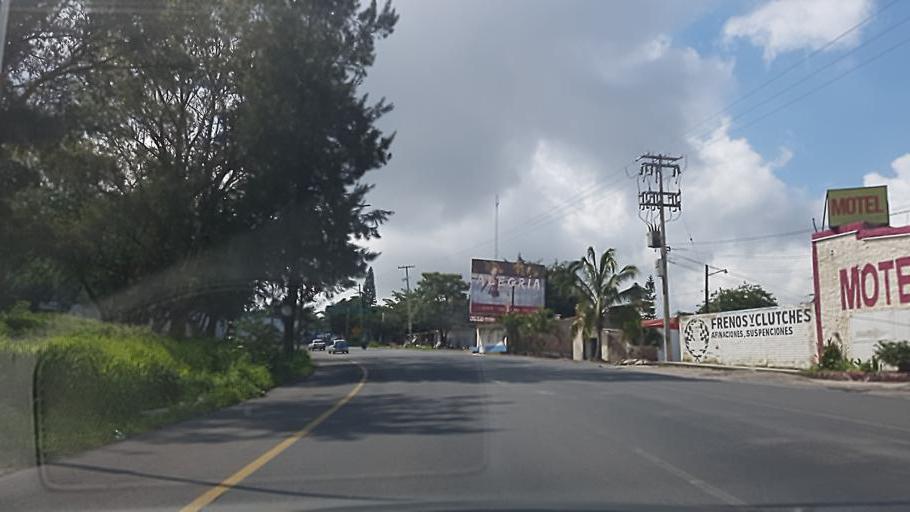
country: MX
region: Nayarit
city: Tepic
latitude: 21.4994
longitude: -104.9098
